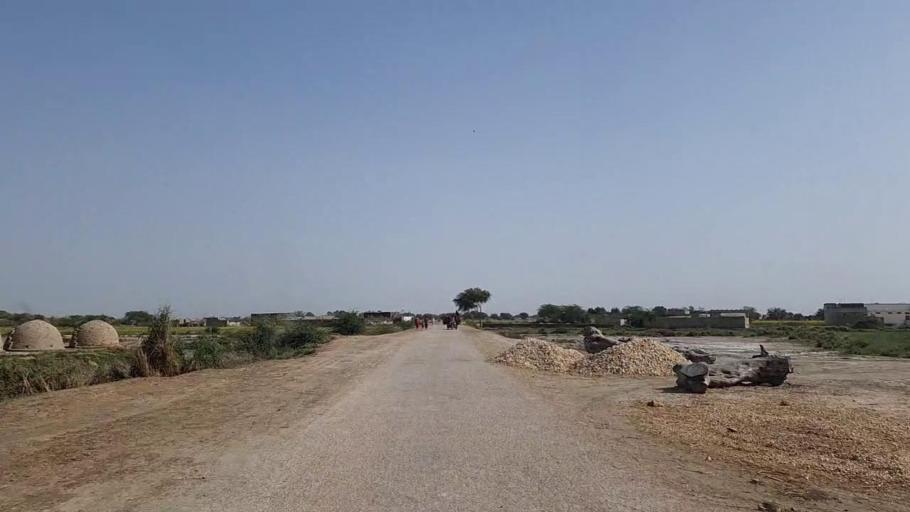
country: PK
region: Sindh
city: Jati
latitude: 24.3558
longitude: 68.2741
